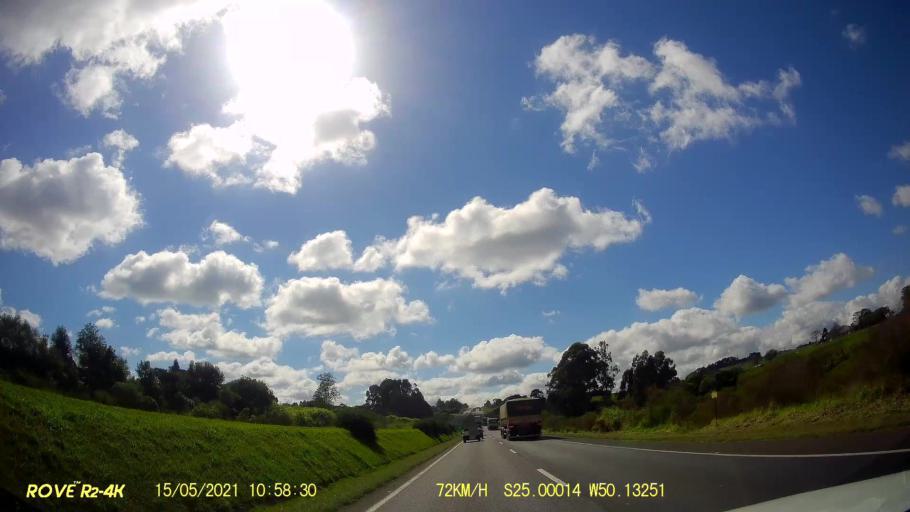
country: BR
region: Parana
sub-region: Carambei
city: Carambei
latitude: -25.0003
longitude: -50.1327
